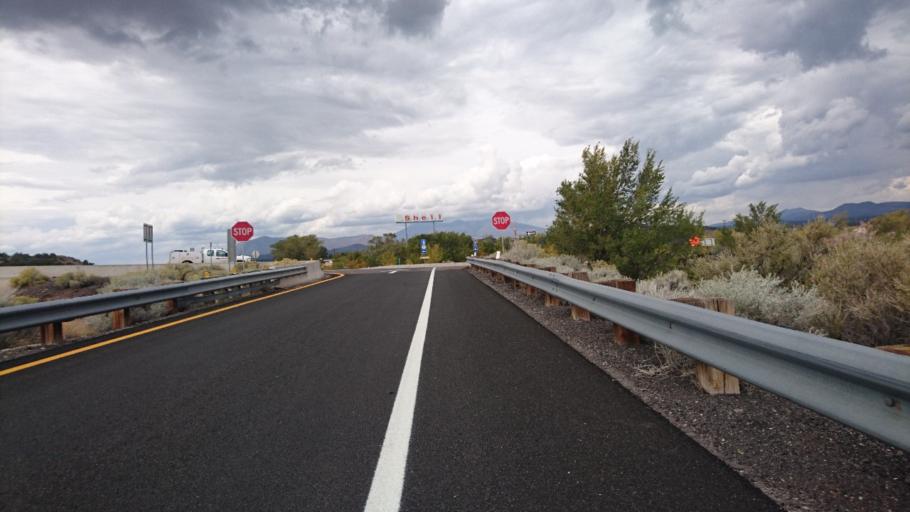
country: US
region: Arizona
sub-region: Coconino County
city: Flagstaff
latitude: 35.2022
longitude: -111.4065
